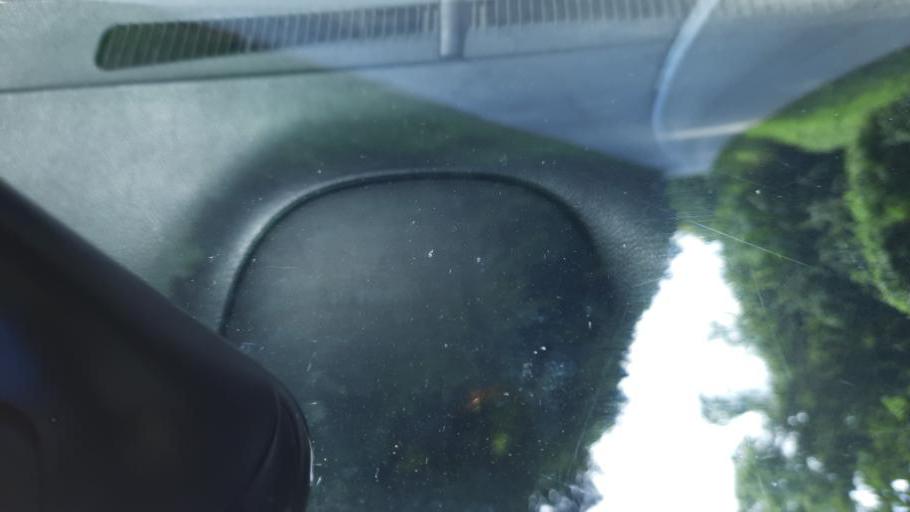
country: RS
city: Glozan
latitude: 45.1427
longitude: 19.5800
